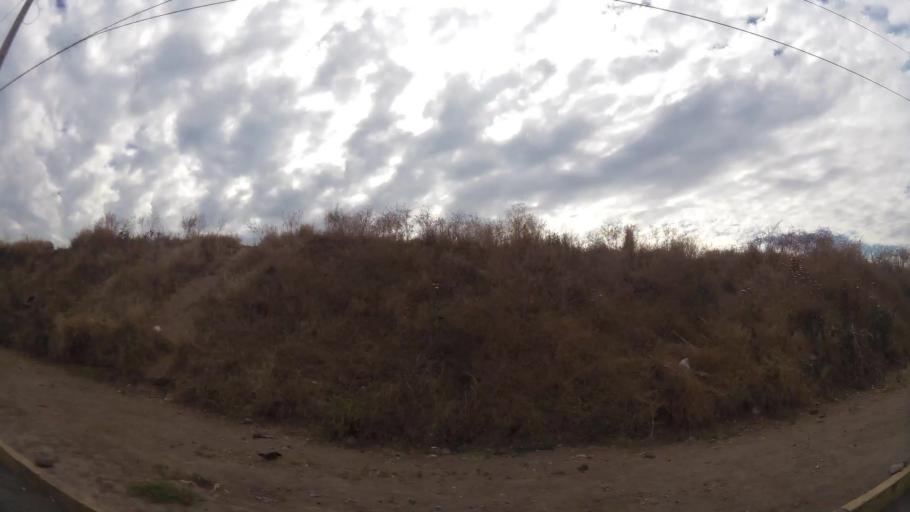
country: CL
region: Santiago Metropolitan
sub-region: Provincia de Santiago
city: La Pintana
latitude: -33.6228
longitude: -70.6179
